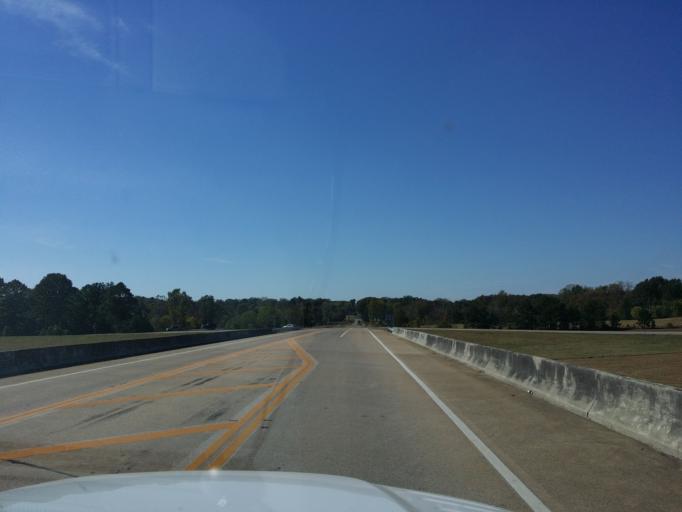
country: US
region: Mississippi
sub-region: Alcorn County
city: Corinth
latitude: 34.9819
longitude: -88.5205
